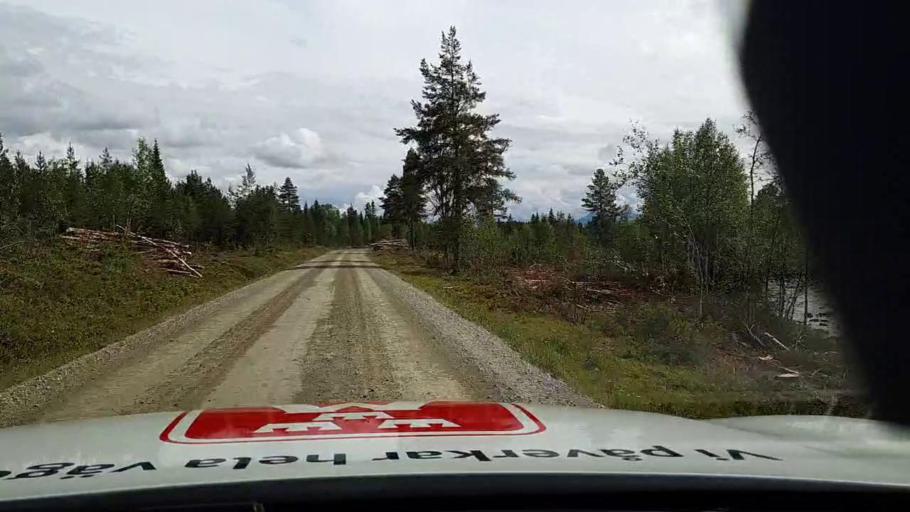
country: SE
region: Jaemtland
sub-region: Are Kommun
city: Jarpen
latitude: 62.5280
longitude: 13.4860
